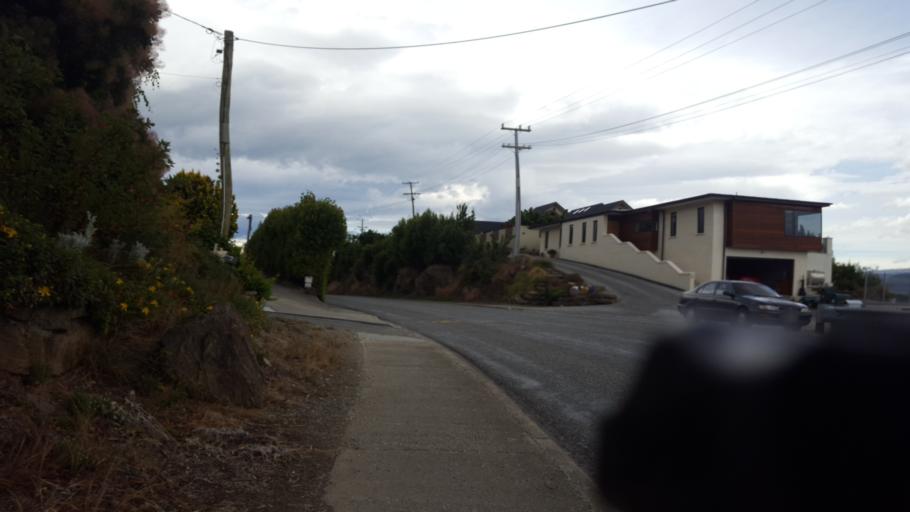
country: NZ
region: Otago
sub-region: Queenstown-Lakes District
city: Wanaka
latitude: -45.2583
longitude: 169.3843
